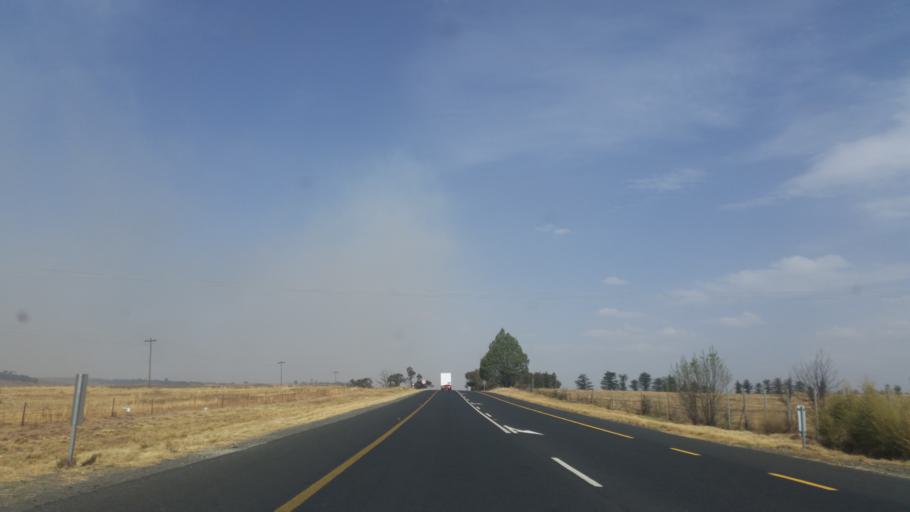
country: ZA
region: Orange Free State
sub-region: Thabo Mofutsanyana District Municipality
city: Bethlehem
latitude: -28.2673
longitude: 28.3633
